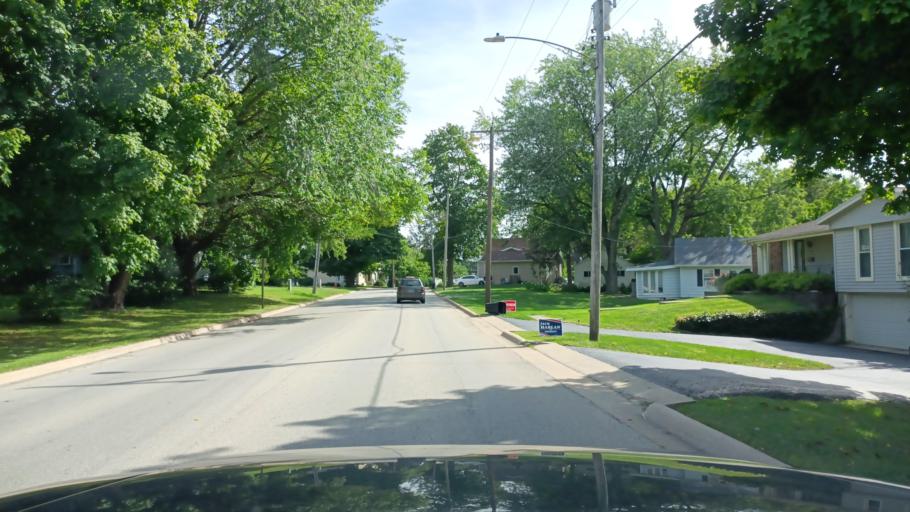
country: US
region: Illinois
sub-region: Knox County
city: Knoxville
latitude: 40.9103
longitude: -90.2900
